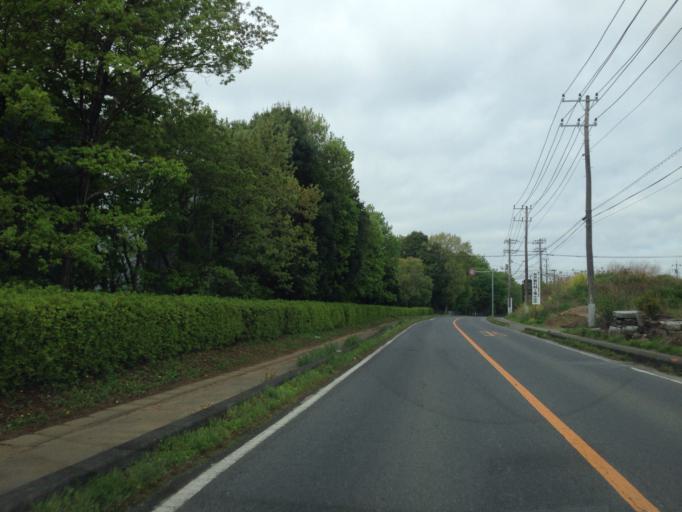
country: JP
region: Ibaraki
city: Tsukuba
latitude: 36.1347
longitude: 140.0773
